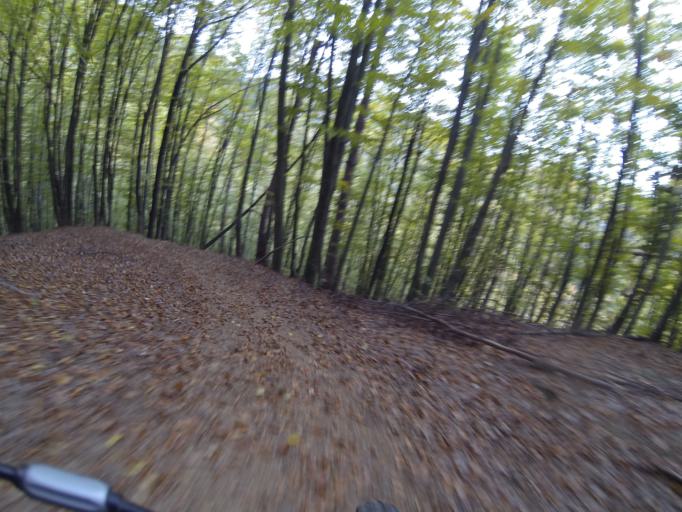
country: RO
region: Gorj
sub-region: Comuna Tismana
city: Sohodol
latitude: 45.0816
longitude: 22.8861
